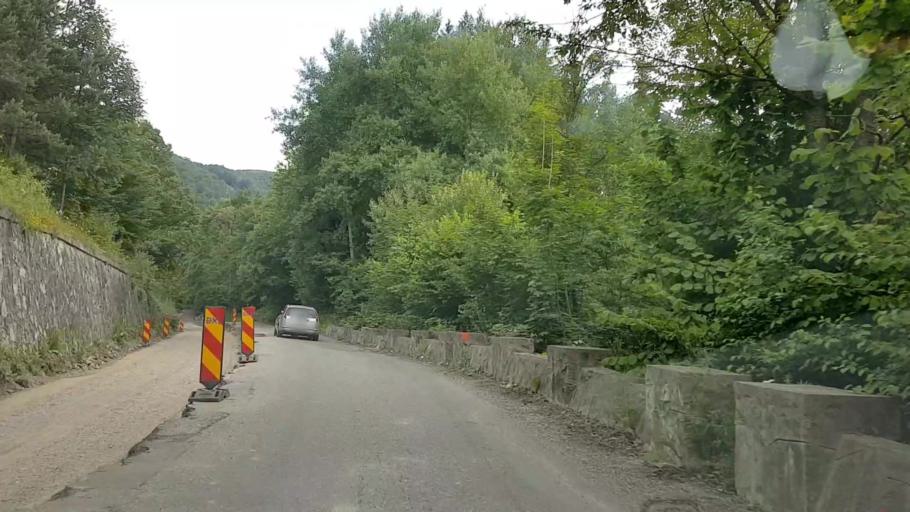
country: RO
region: Neamt
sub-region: Comuna Pangarati
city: Pangarati
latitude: 46.9417
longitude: 26.1245
